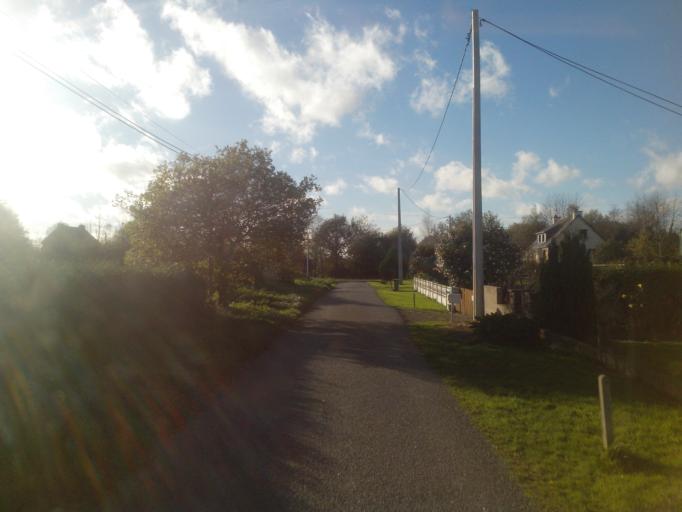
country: FR
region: Brittany
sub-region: Departement du Morbihan
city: Guilliers
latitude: 48.1086
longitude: -2.4016
